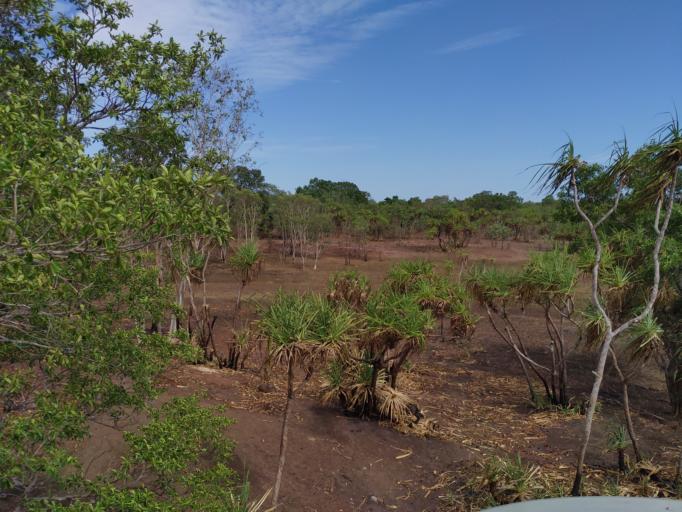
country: AU
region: Northern Territory
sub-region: Litchfield
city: McMinns Lagoon
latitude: -12.5572
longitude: 131.2978
